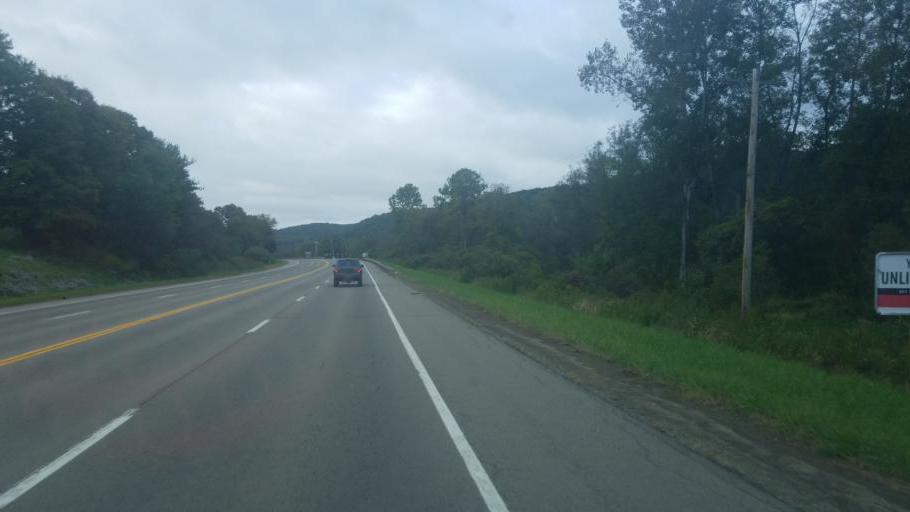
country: US
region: New York
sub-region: Cattaraugus County
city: Weston Mills
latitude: 42.1658
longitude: -78.3933
